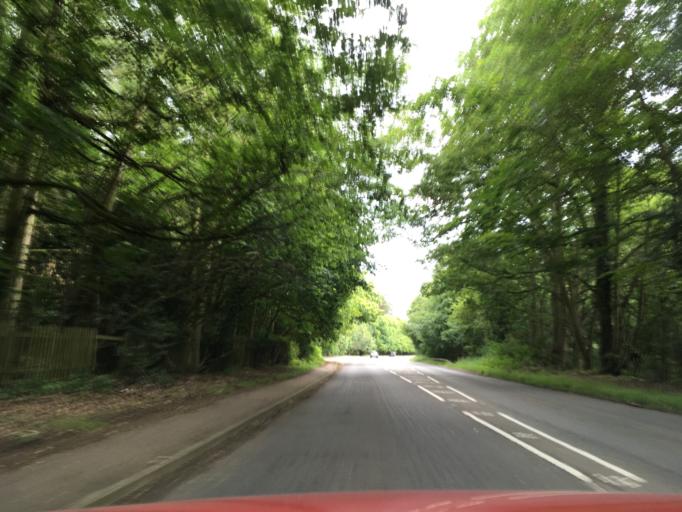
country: GB
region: England
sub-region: Milton Keynes
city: Woburn Sands
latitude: 52.0076
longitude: -0.6444
